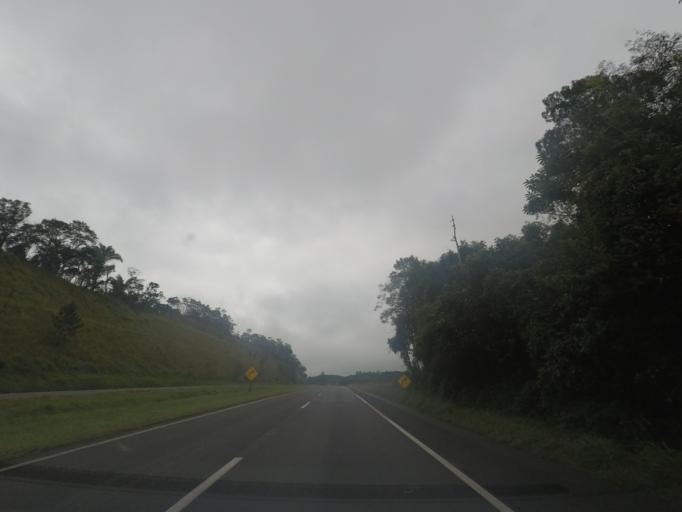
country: BR
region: Parana
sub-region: Antonina
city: Antonina
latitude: -25.0947
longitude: -48.6517
